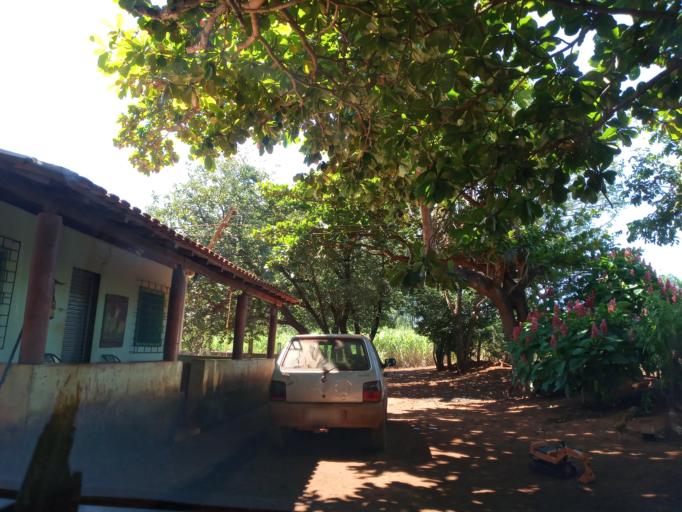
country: BR
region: Goias
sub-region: Itumbiara
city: Itumbiara
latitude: -18.4372
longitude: -49.1461
